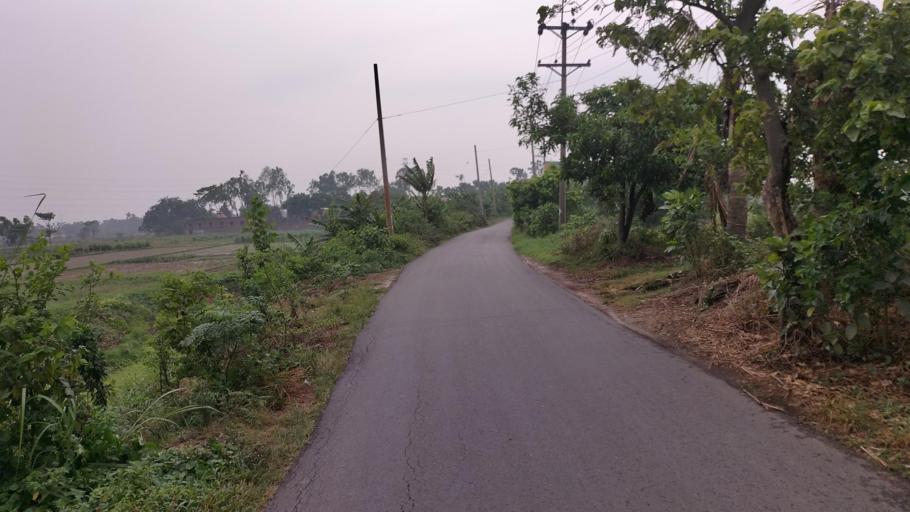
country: BD
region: Dhaka
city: Azimpur
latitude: 23.6790
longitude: 90.3490
